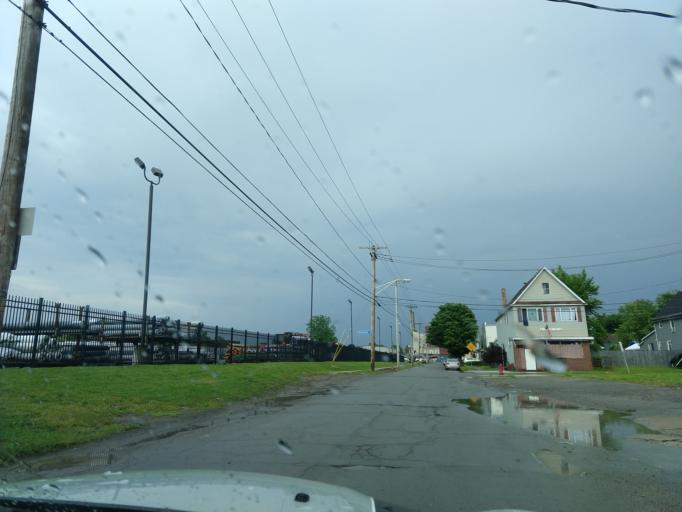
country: US
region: New York
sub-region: Erie County
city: Kenmore
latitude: 42.9433
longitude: -78.8838
